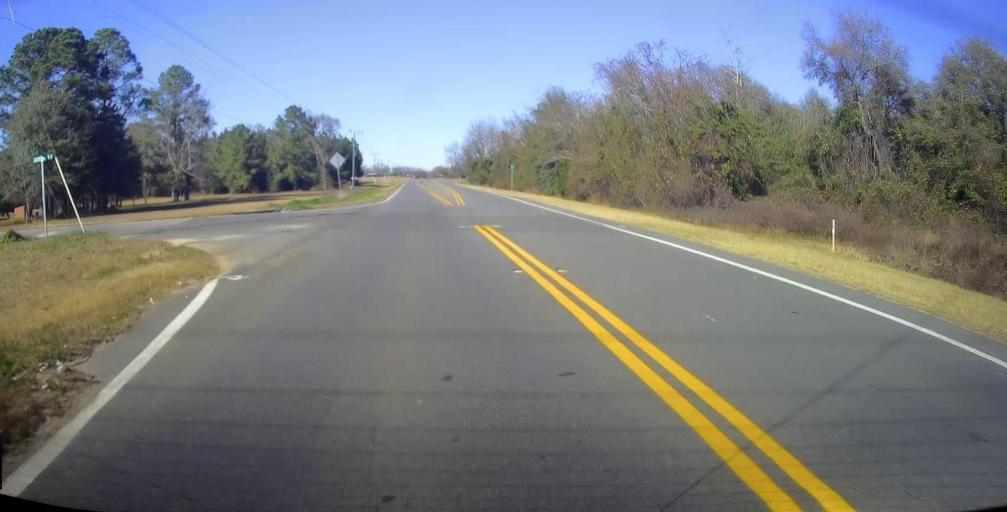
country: US
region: Georgia
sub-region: Macon County
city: Oglethorpe
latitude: 32.2541
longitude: -84.0858
